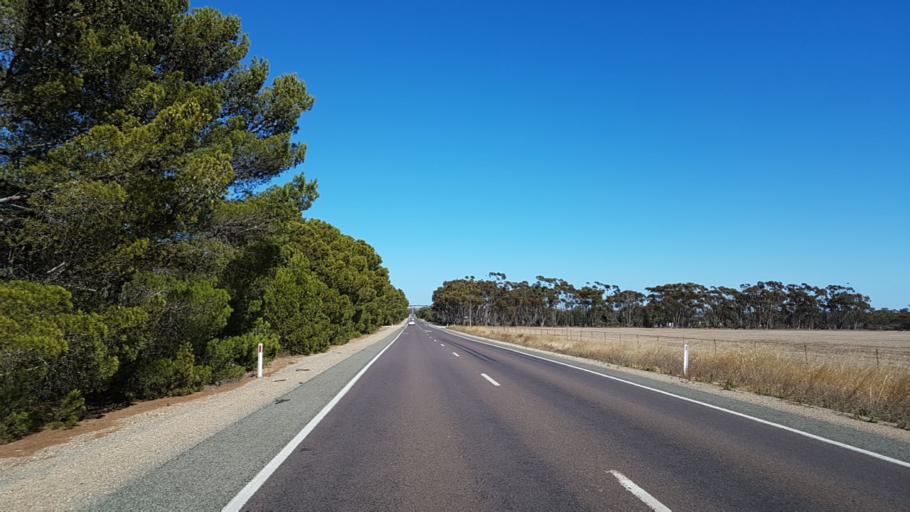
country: AU
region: South Australia
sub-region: Copper Coast
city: Kadina
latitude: -34.0579
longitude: 138.0257
